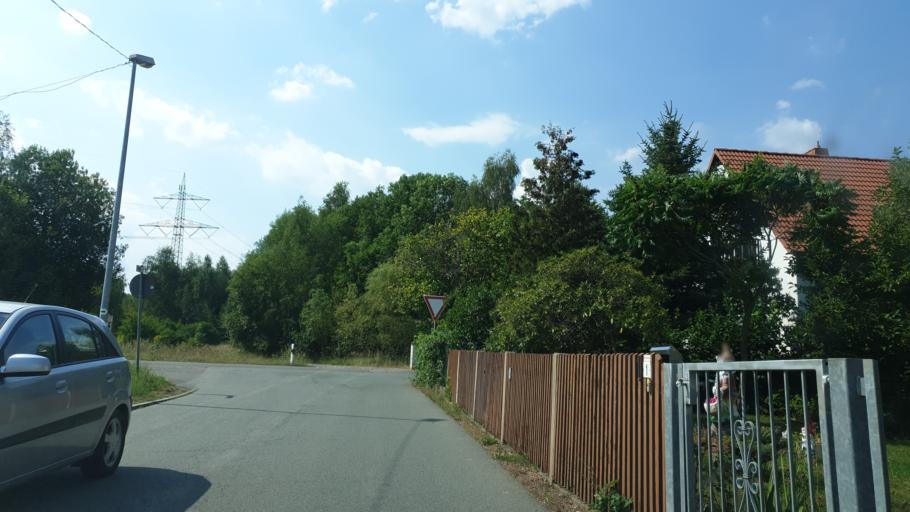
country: DE
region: Saxony
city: Neukirchen
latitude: 50.7817
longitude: 12.8850
